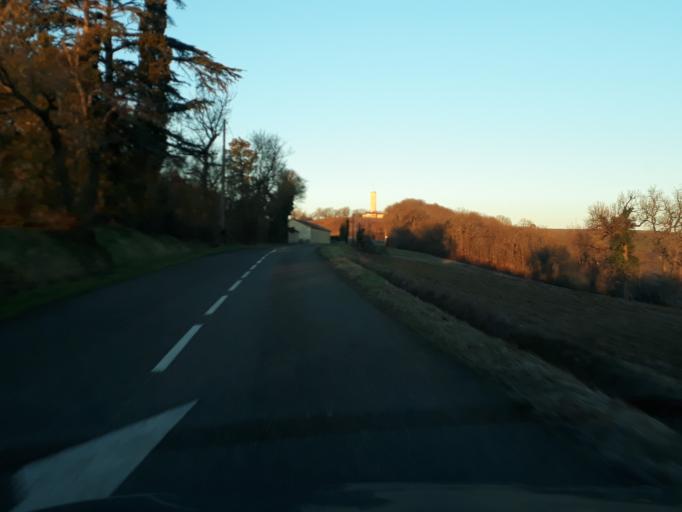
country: FR
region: Midi-Pyrenees
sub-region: Departement du Gers
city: Aubiet
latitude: 43.6008
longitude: 0.7055
